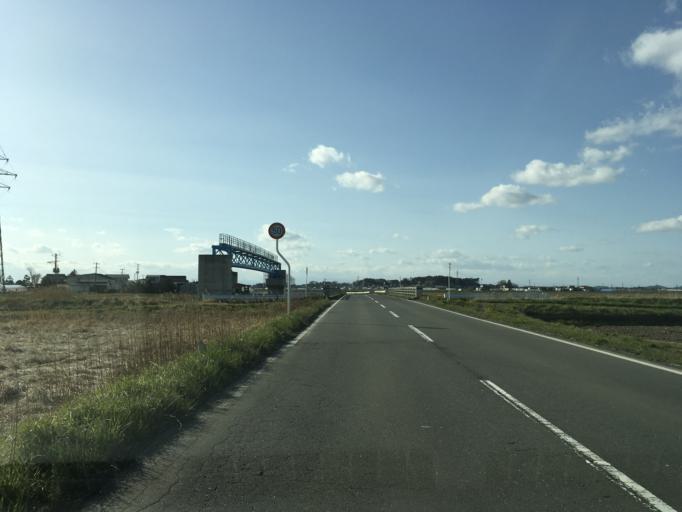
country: JP
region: Miyagi
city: Wakuya
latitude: 38.6572
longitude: 141.2334
